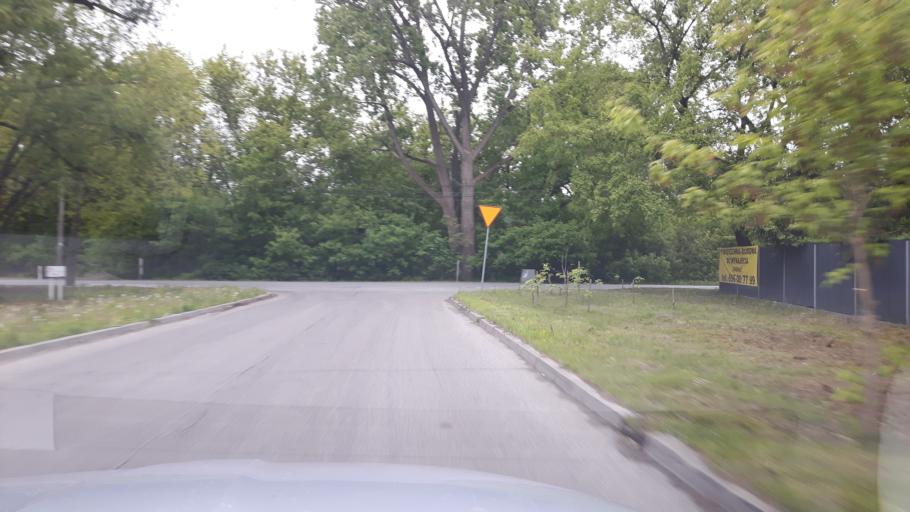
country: PL
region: Masovian Voivodeship
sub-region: Warszawa
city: Rembertow
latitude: 52.2598
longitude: 21.1357
